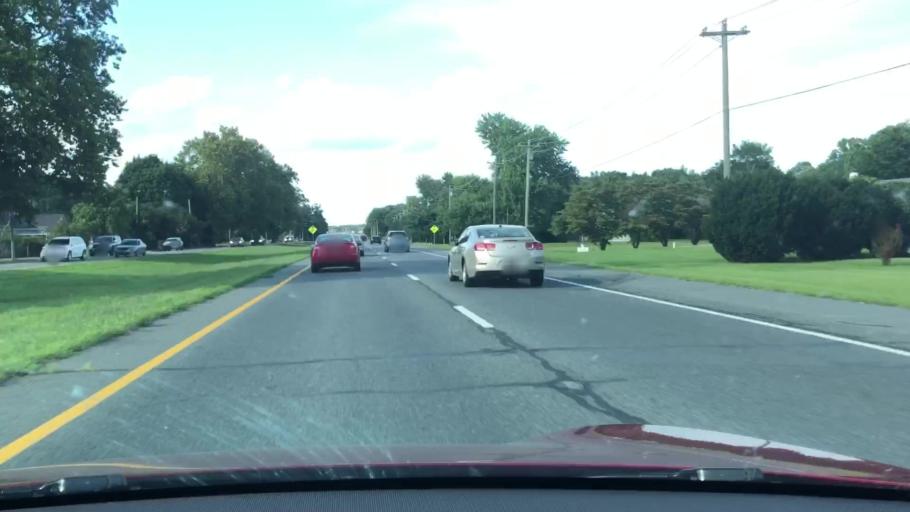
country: US
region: Delaware
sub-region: Kent County
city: Felton
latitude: 39.0314
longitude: -75.5616
